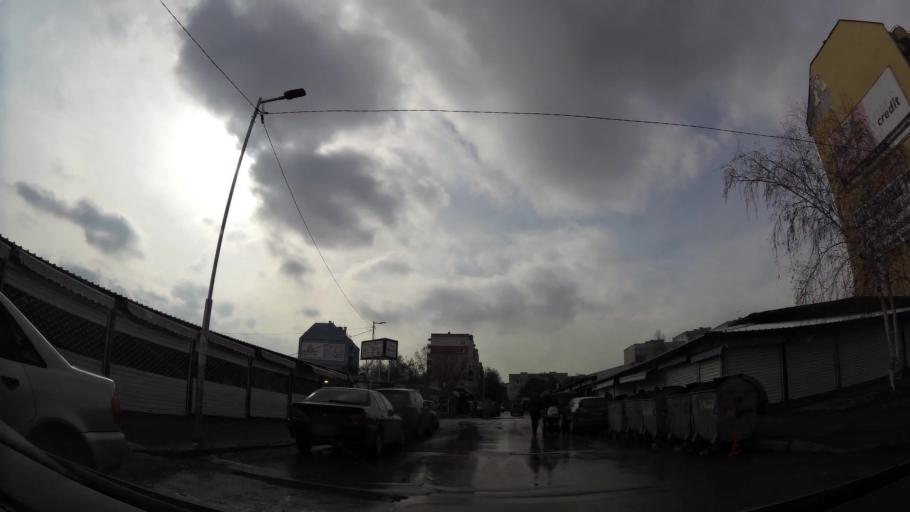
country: BG
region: Sofiya
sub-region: Obshtina Bozhurishte
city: Bozhurishte
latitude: 42.7192
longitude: 23.2518
